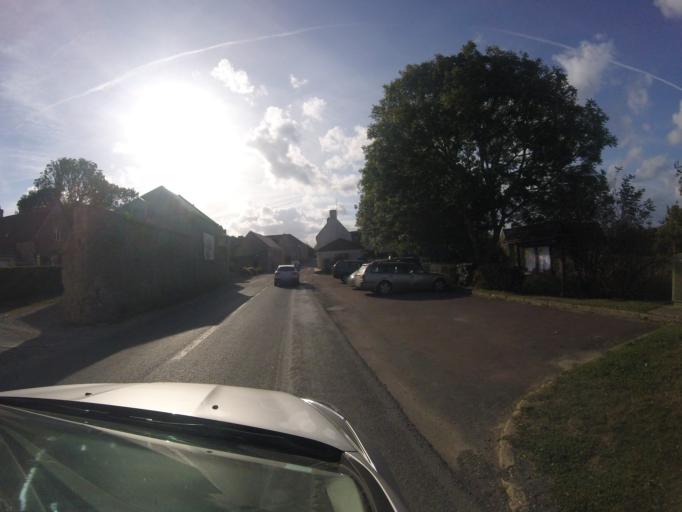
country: FR
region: Lower Normandy
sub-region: Departement du Calvados
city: Port-en-Bessin-Huppain
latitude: 49.3485
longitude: -0.8462
